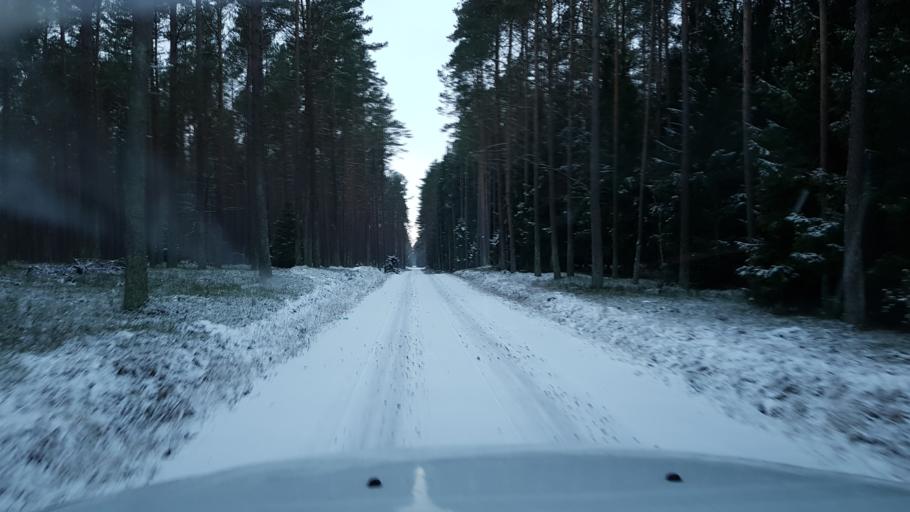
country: PL
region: West Pomeranian Voivodeship
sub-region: Powiat drawski
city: Wierzchowo
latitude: 53.4805
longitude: 16.1560
